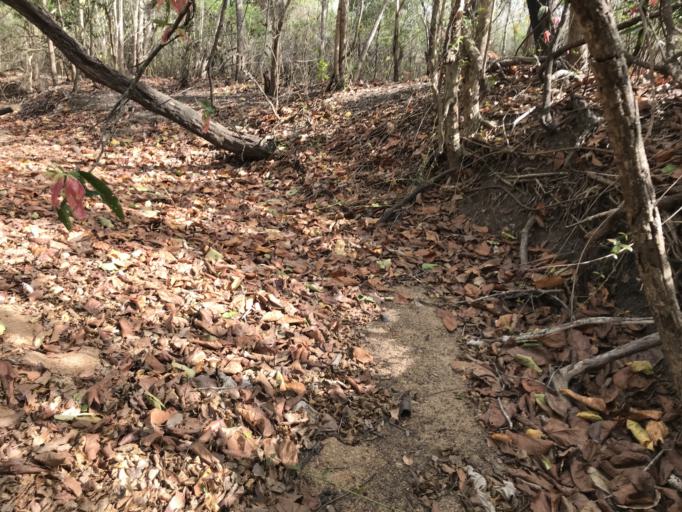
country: LK
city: Padaviya Divisional Secretariat
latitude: 9.0854
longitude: 80.8048
